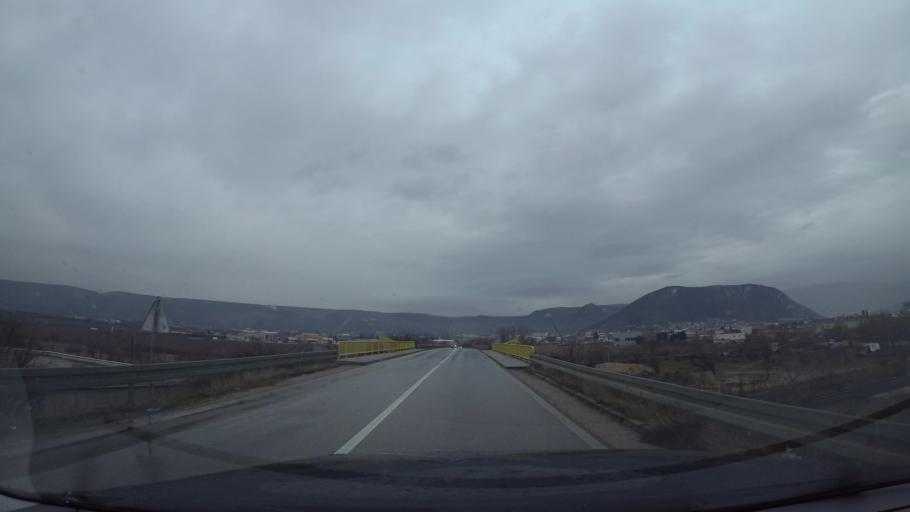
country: BA
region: Federation of Bosnia and Herzegovina
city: Rodoc
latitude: 43.3017
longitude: 17.8380
